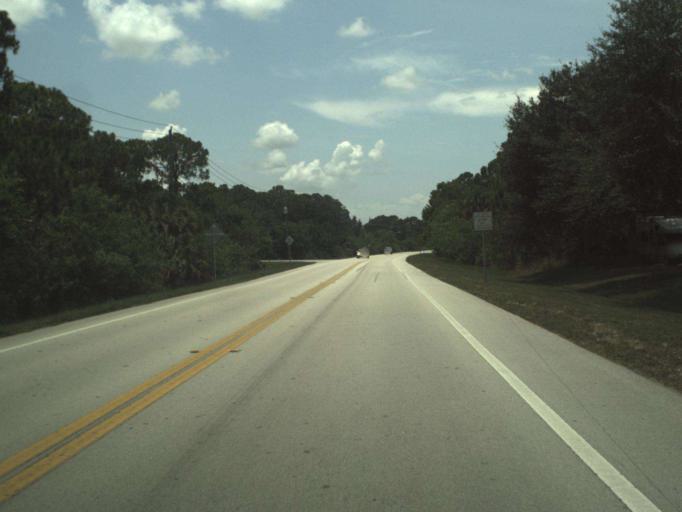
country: US
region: Florida
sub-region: Saint Lucie County
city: Lakewood Park
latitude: 27.5451
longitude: -80.3761
